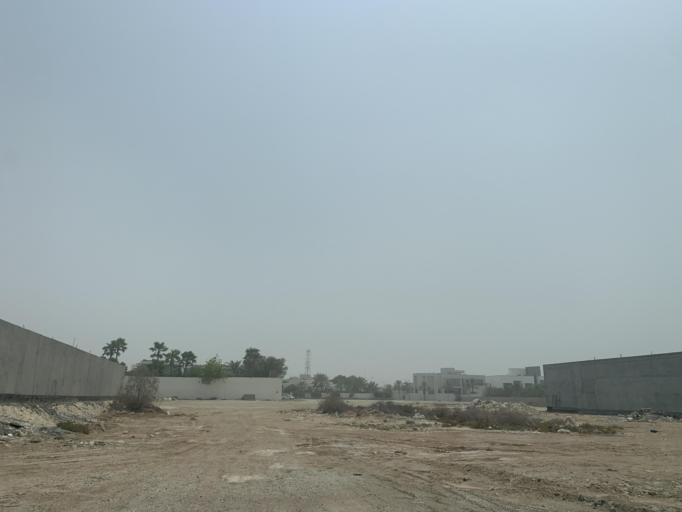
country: BH
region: Central Governorate
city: Madinat Hamad
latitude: 26.1654
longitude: 50.4749
